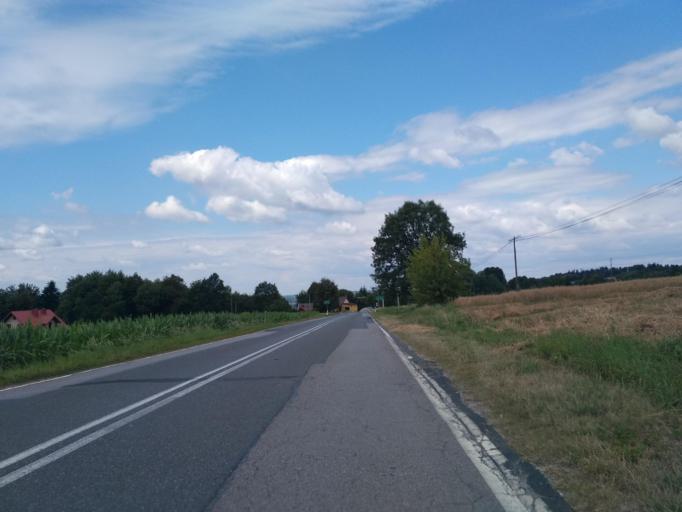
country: PL
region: Subcarpathian Voivodeship
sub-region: Powiat rzeszowski
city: Hyzne
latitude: 49.8956
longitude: 22.2280
